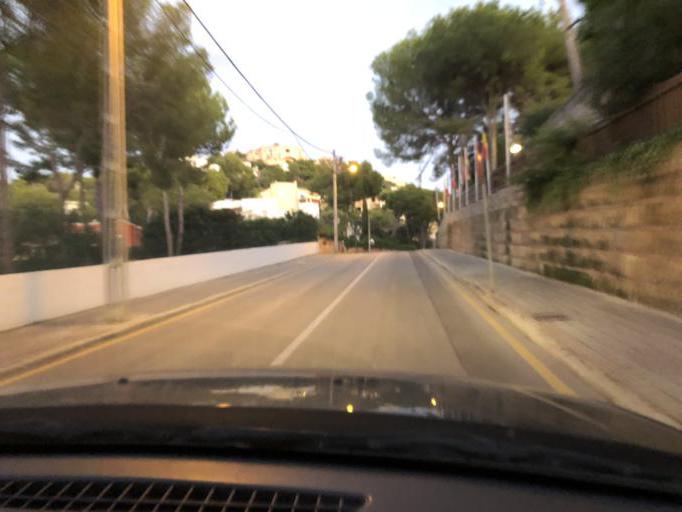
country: ES
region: Balearic Islands
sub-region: Illes Balears
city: Santa Ponsa
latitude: 39.5213
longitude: 2.4750
